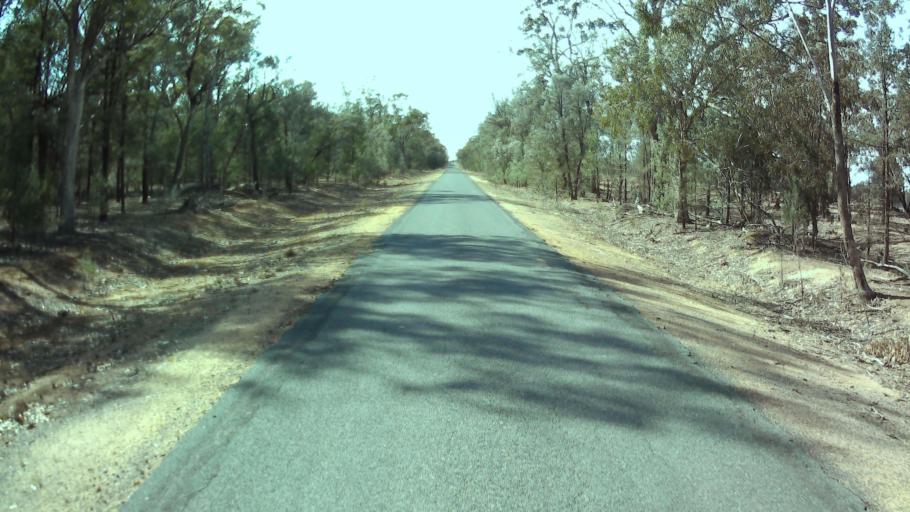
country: AU
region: New South Wales
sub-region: Weddin
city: Grenfell
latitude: -33.7259
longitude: 148.0318
